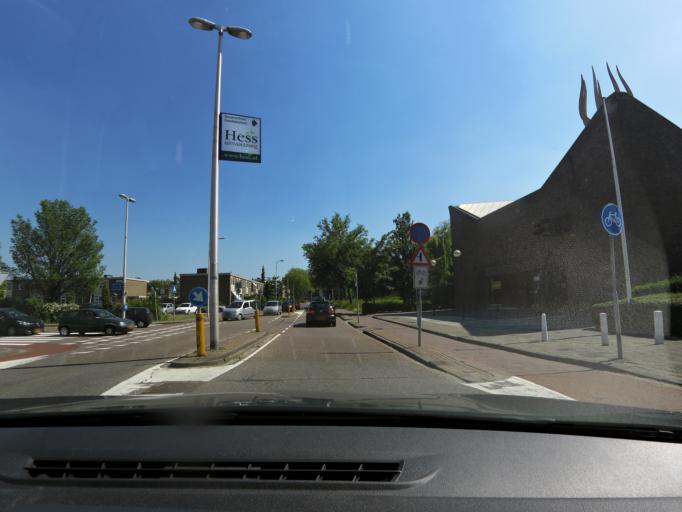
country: NL
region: South Holland
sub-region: Gemeente Capelle aan den IJssel
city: Capelle aan den IJssel
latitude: 51.9286
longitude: 4.5898
